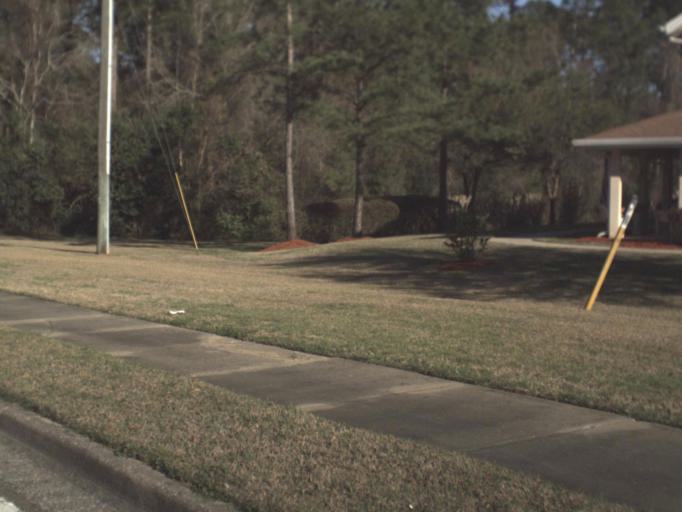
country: US
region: Florida
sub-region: Leon County
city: Tallahassee
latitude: 30.4559
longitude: -84.2394
